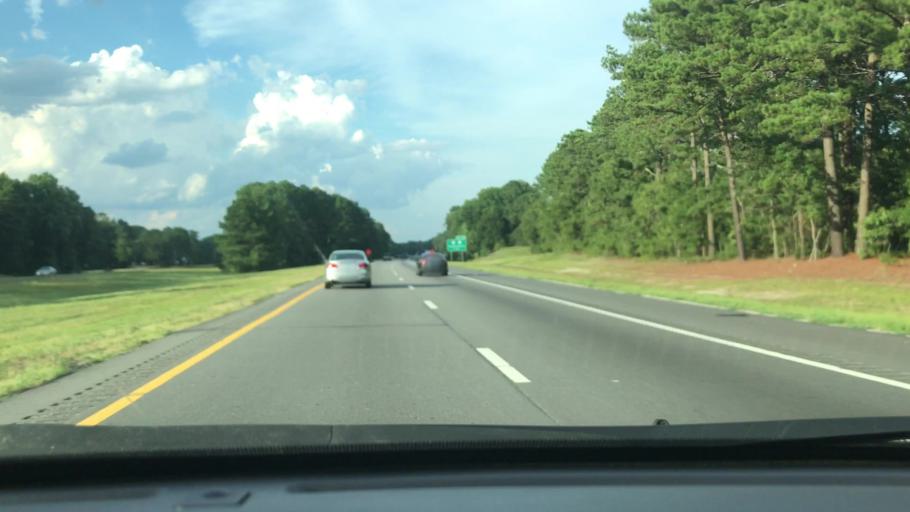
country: US
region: North Carolina
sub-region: Cumberland County
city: Vander
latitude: 34.9905
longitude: -78.8367
